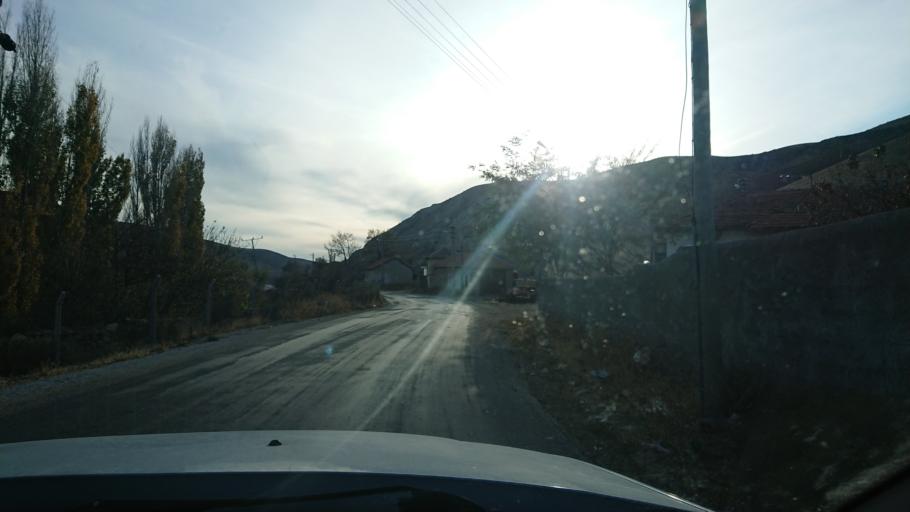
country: TR
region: Ankara
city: Sereflikochisar
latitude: 38.7644
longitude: 33.6991
